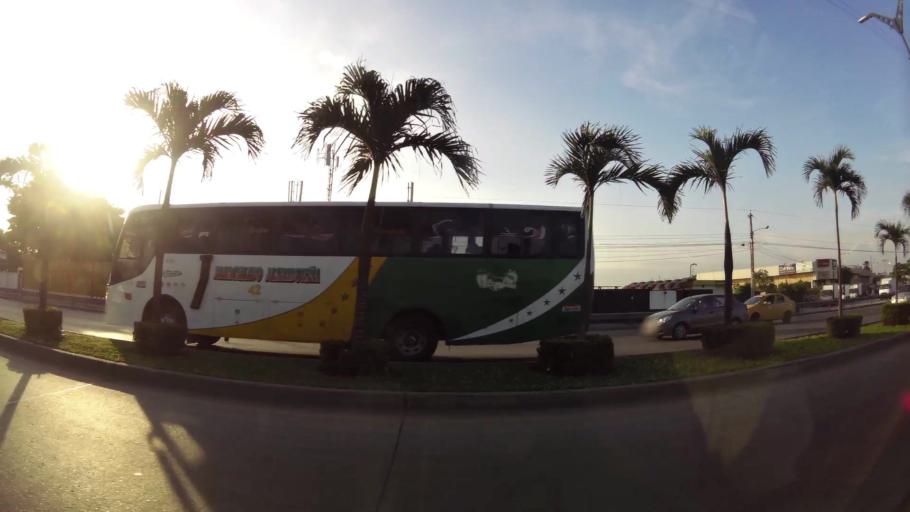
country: EC
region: Guayas
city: Eloy Alfaro
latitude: -2.1510
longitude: -79.8771
